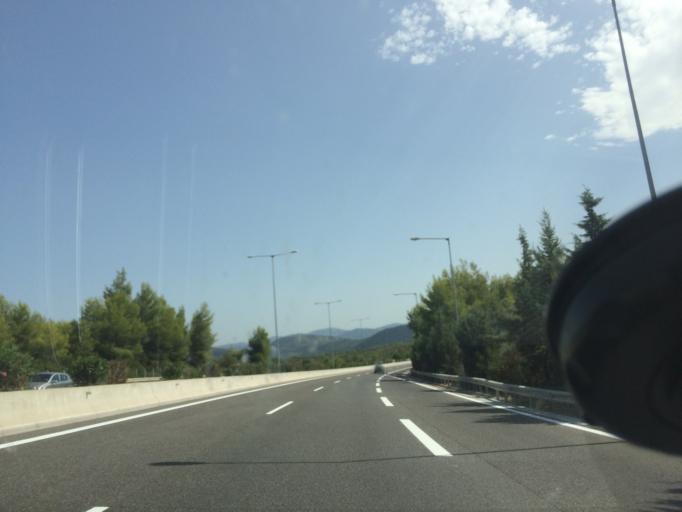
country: GR
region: Central Greece
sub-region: Nomos Fthiotidos
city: Martinon
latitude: 38.5941
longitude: 23.1961
